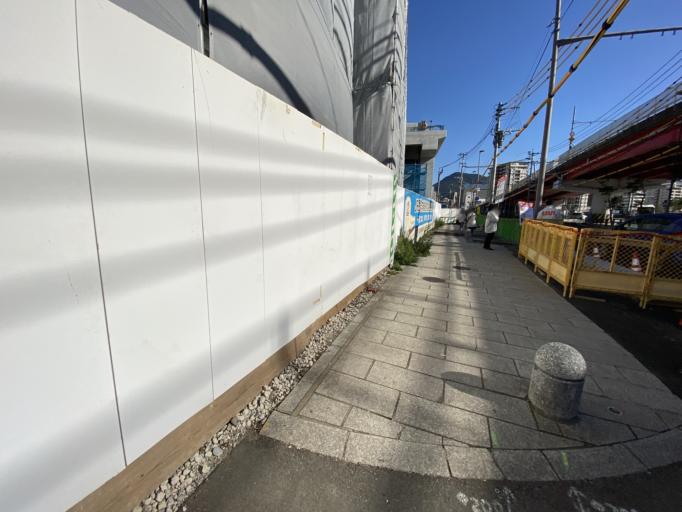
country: JP
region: Nagasaki
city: Nagasaki-shi
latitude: 32.7513
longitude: 129.8685
